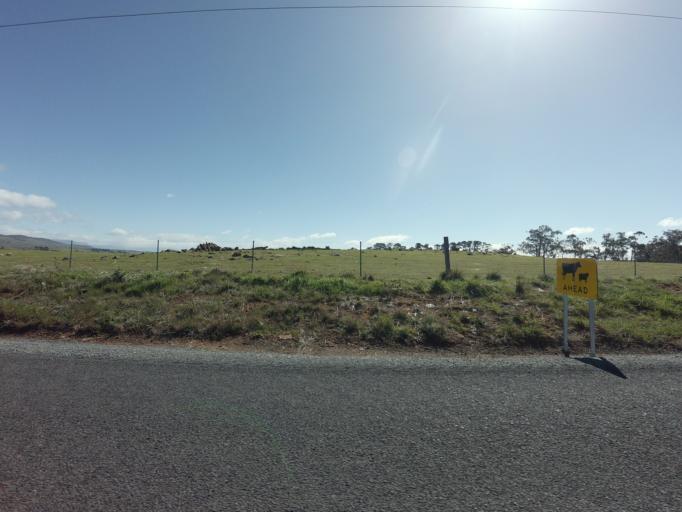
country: AU
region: Tasmania
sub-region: Northern Midlands
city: Evandale
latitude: -41.9088
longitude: 147.3851
